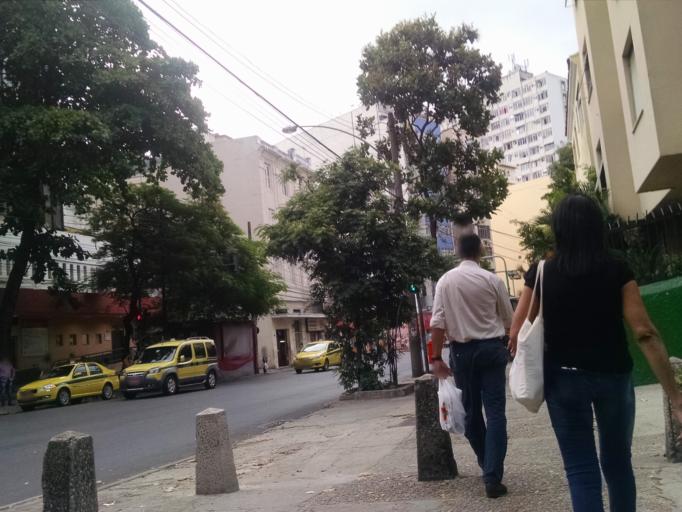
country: BR
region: Rio de Janeiro
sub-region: Rio De Janeiro
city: Rio de Janeiro
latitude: -22.9374
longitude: -43.1903
